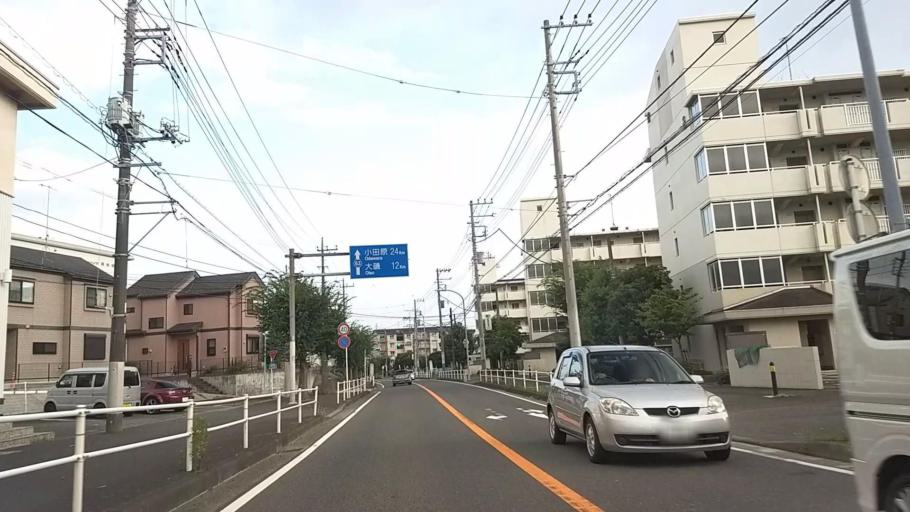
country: JP
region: Kanagawa
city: Isehara
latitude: 35.3979
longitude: 139.2995
